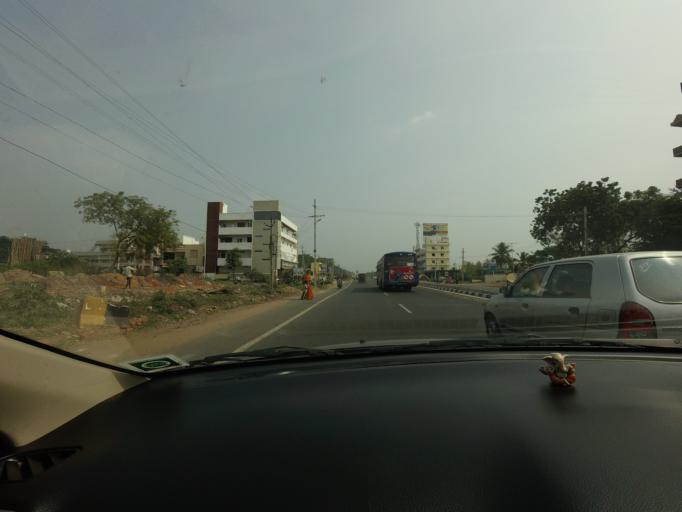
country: IN
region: Andhra Pradesh
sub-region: Krishna
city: Yanamalakuduru
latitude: 16.4830
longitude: 80.6880
